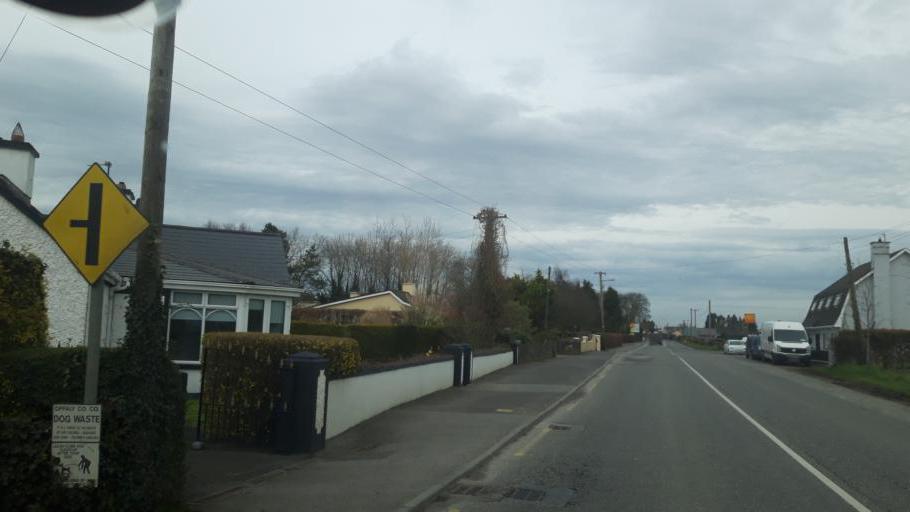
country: IE
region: Leinster
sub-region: Uibh Fhaili
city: Edenderry
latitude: 53.3312
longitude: -7.0728
